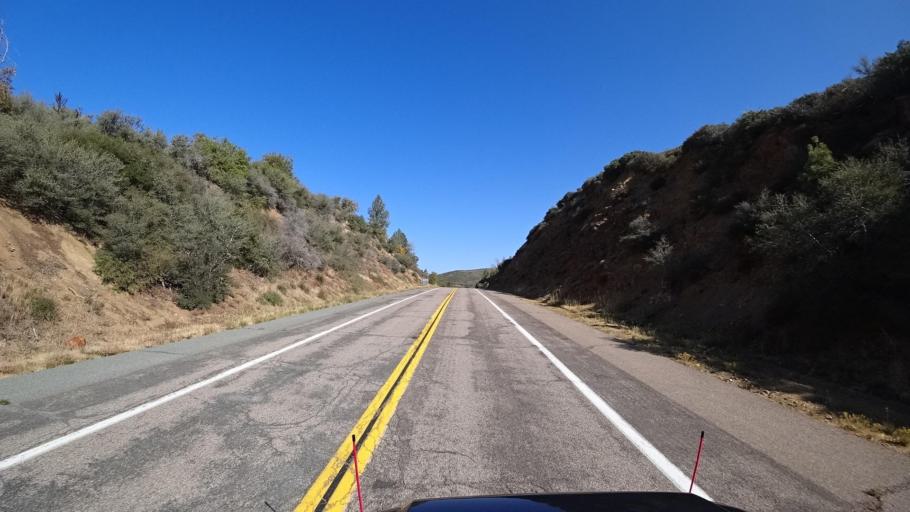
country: US
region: California
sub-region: San Diego County
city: Pine Valley
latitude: 32.9288
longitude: -116.4847
